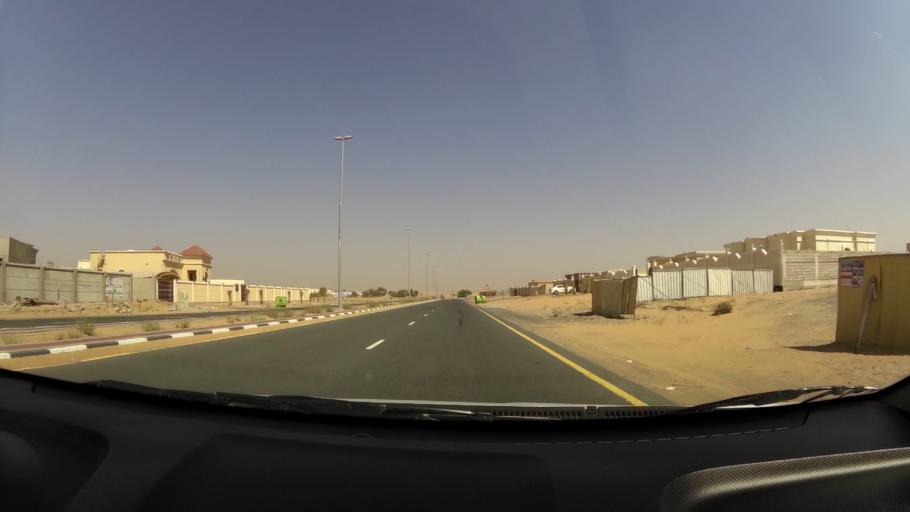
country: AE
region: Umm al Qaywayn
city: Umm al Qaywayn
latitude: 25.4749
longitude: 55.6066
